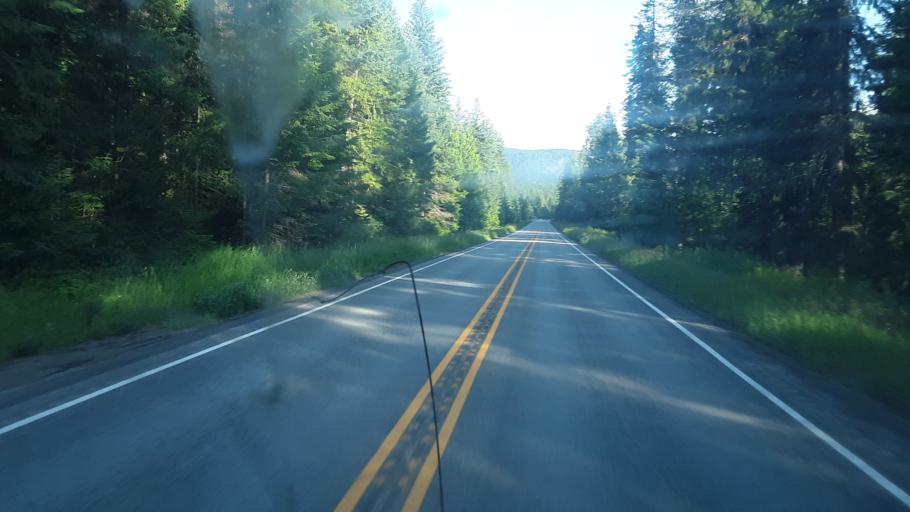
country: US
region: Idaho
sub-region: Boundary County
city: Bonners Ferry
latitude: 48.6037
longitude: -116.0089
